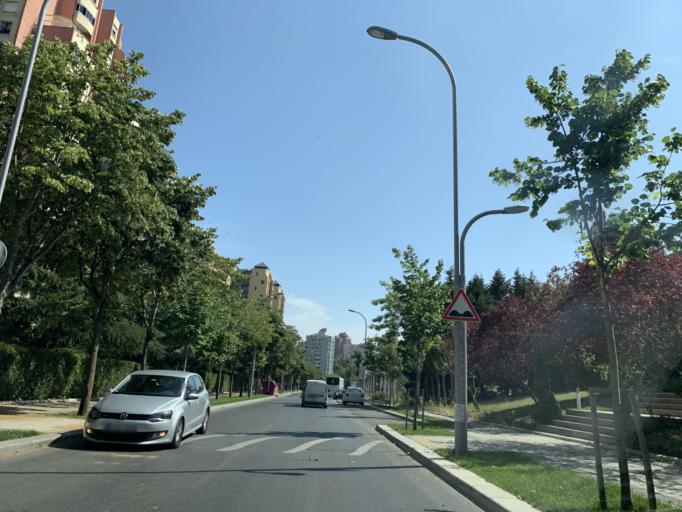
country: TR
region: Istanbul
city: Esenyurt
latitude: 41.0703
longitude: 28.6782
